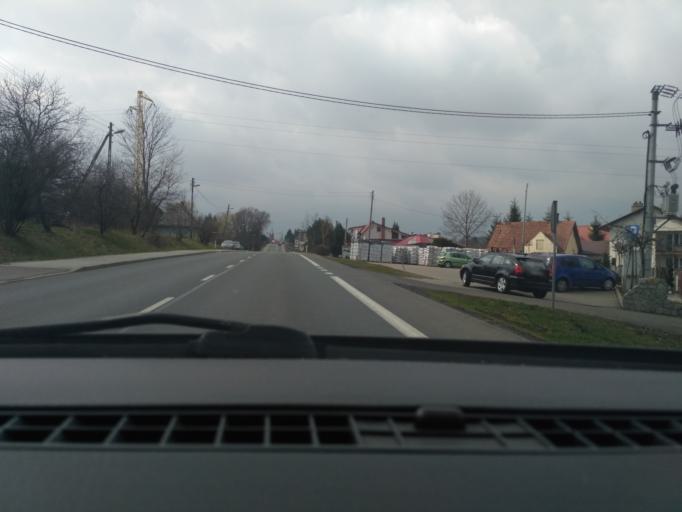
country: PL
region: Subcarpathian Voivodeship
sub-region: Powiat krosnienski
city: Miejsce Piastowe
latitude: 49.6377
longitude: 21.7931
